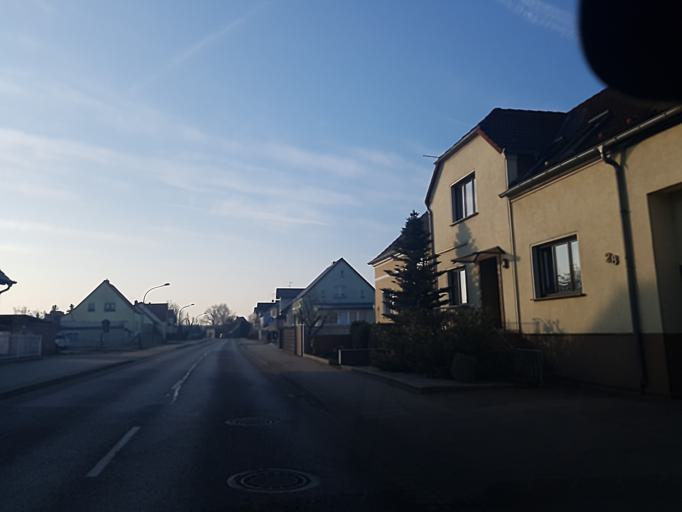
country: DE
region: Brandenburg
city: Golzow
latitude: 52.2737
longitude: 12.5977
